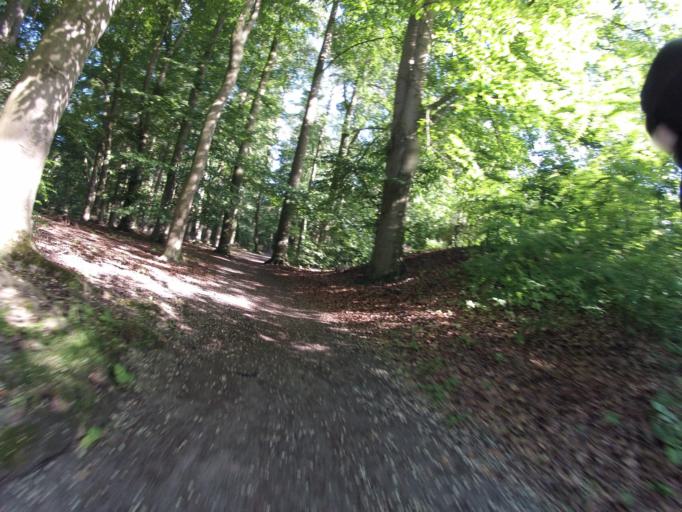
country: DE
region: North Rhine-Westphalia
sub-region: Regierungsbezirk Munster
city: Horstel
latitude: 52.2749
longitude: 7.6016
